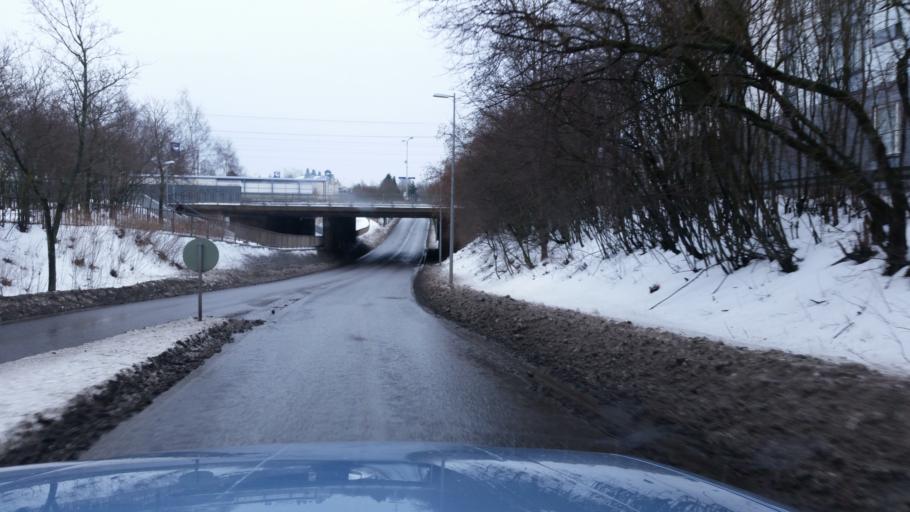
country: FI
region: Uusimaa
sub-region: Helsinki
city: Vantaa
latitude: 60.2776
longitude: 25.0356
